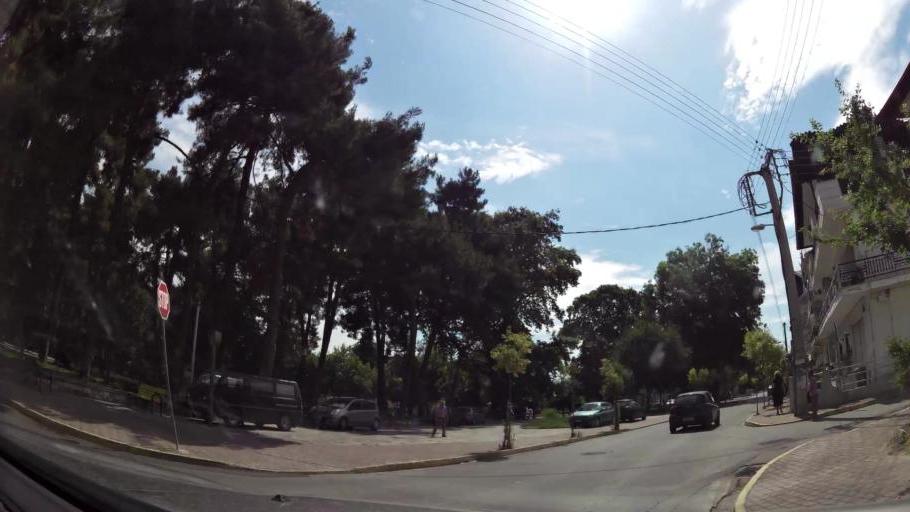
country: GR
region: Central Macedonia
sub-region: Nomos Pierias
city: Katerini
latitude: 40.2699
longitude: 22.4978
